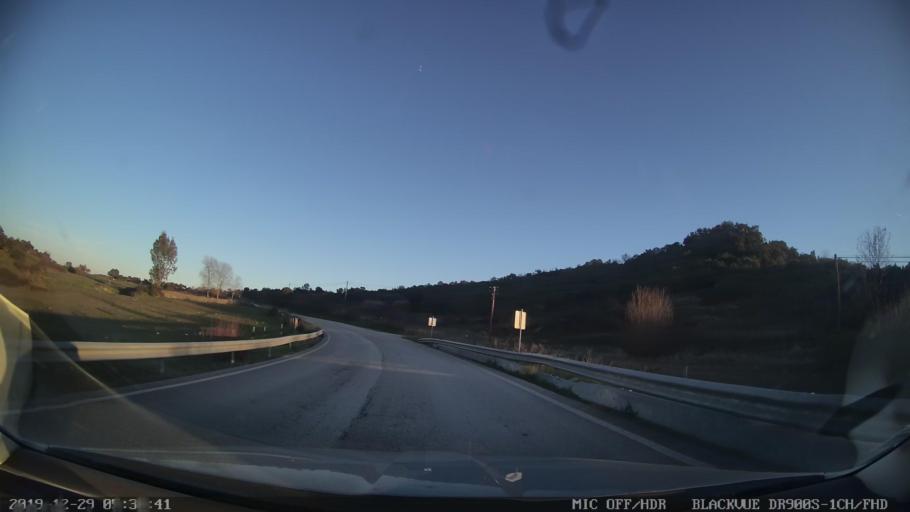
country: PT
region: Castelo Branco
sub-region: Idanha-A-Nova
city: Idanha-a-Nova
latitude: 39.9725
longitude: -7.3417
